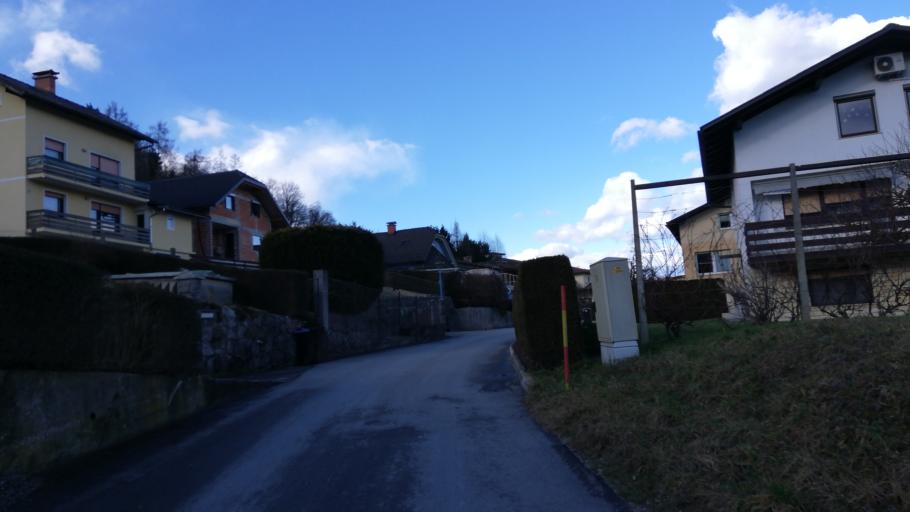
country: SI
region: Medvode
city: Medvode
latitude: 46.1301
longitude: 14.4109
